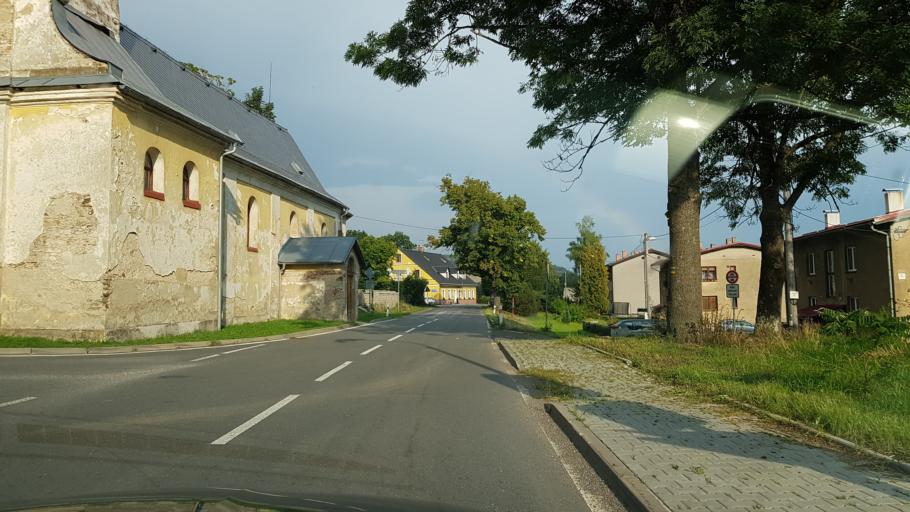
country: CZ
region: Pardubicky
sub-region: Okres Usti nad Orlici
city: Kraliky
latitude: 50.1013
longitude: 16.8003
